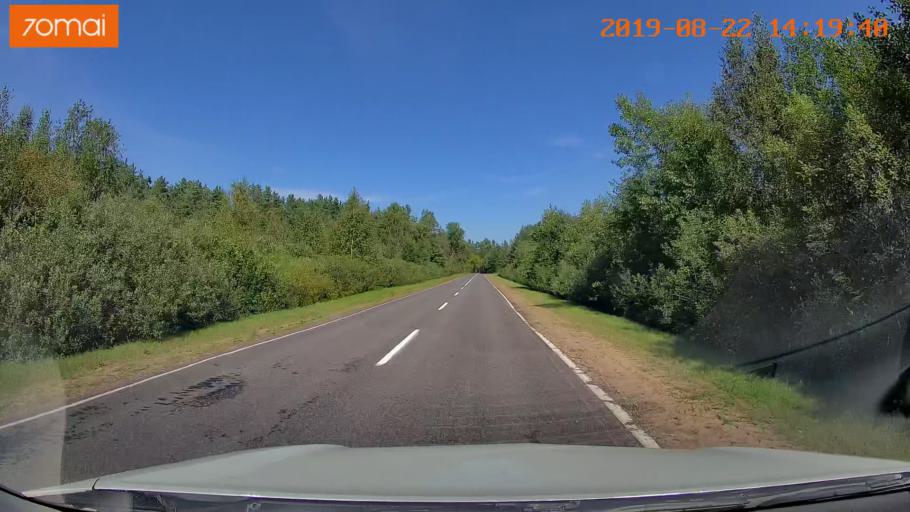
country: BY
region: Mogilev
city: Asipovichy
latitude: 53.2617
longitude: 28.5081
